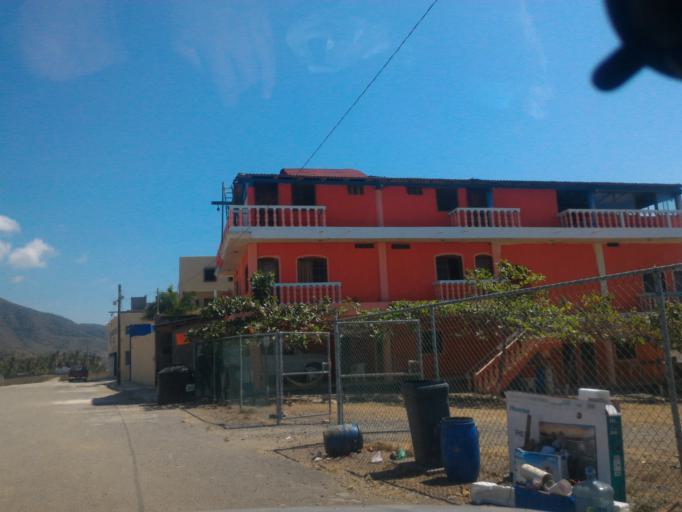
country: MX
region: Michoacan
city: Coahuayana Viejo
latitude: 18.5886
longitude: -103.6828
